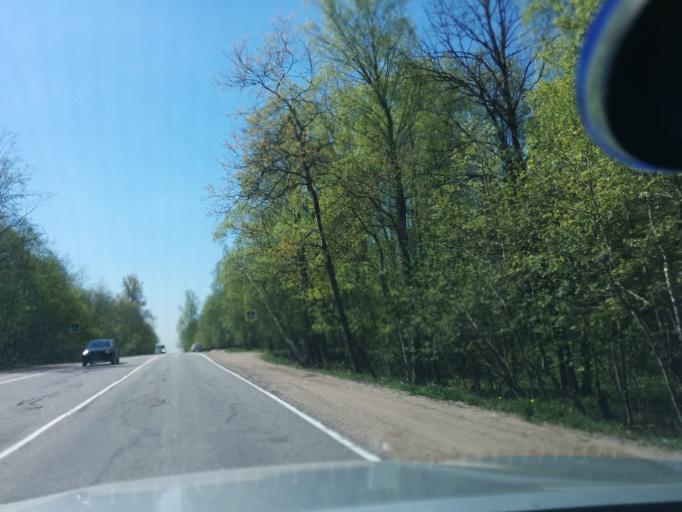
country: RU
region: Leningrad
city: Verkhniye Osel'ki
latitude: 60.2415
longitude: 30.4422
